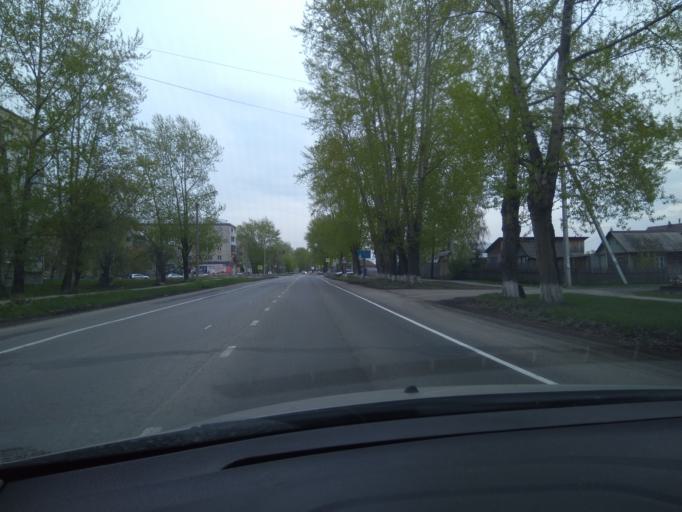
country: RU
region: Sverdlovsk
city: Bogdanovich
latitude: 56.7714
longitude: 62.0431
